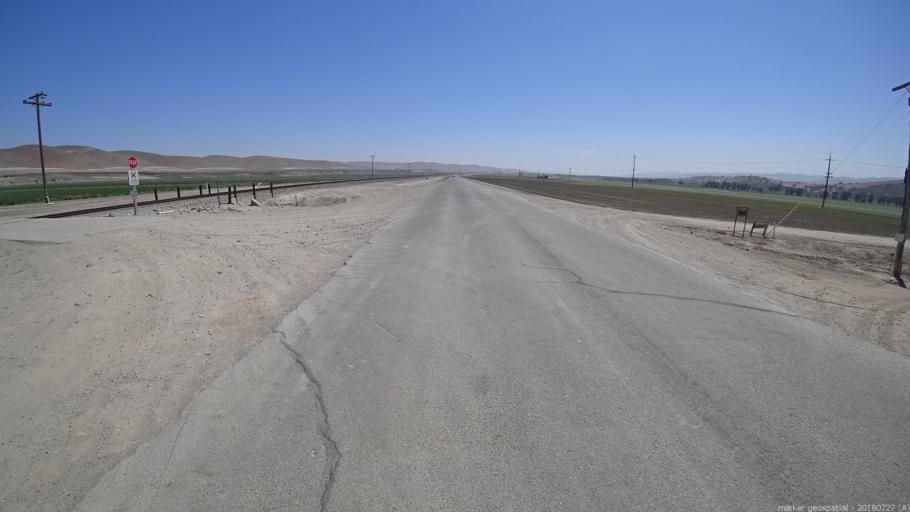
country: US
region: California
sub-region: Monterey County
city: King City
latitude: 36.0943
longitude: -120.9624
